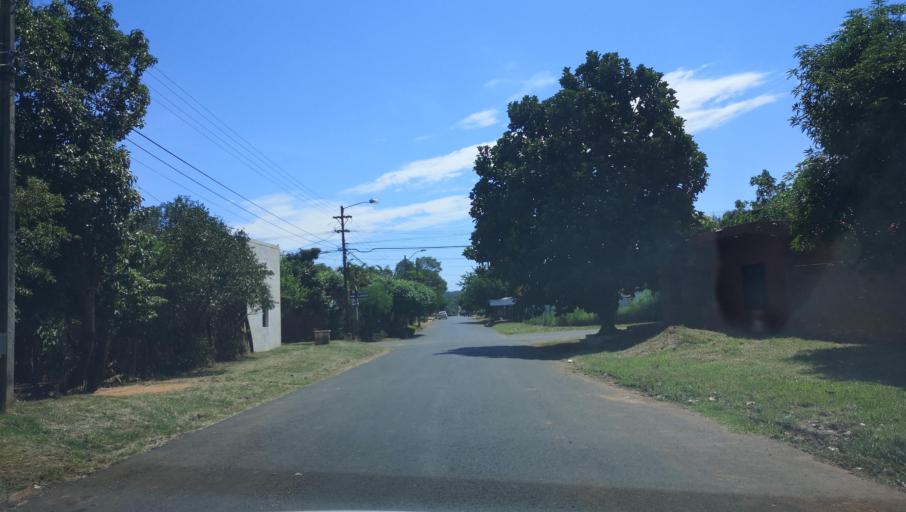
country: PY
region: Misiones
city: Santa Maria
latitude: -26.8921
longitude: -57.0296
